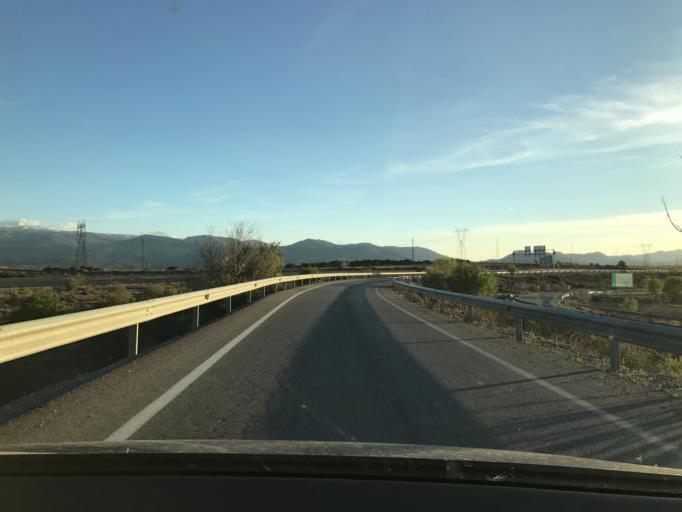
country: ES
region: Andalusia
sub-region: Provincia de Granada
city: Darro
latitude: 37.3227
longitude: -3.2702
